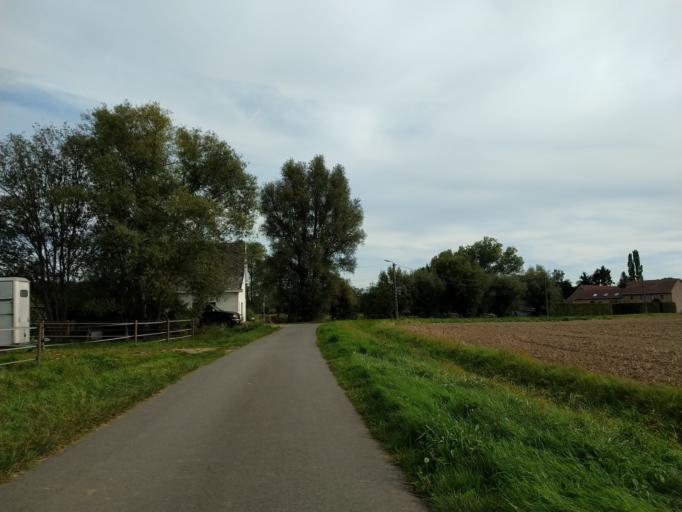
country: BE
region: Flanders
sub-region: Provincie Vlaams-Brabant
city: Haacht
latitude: 50.9611
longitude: 4.6740
